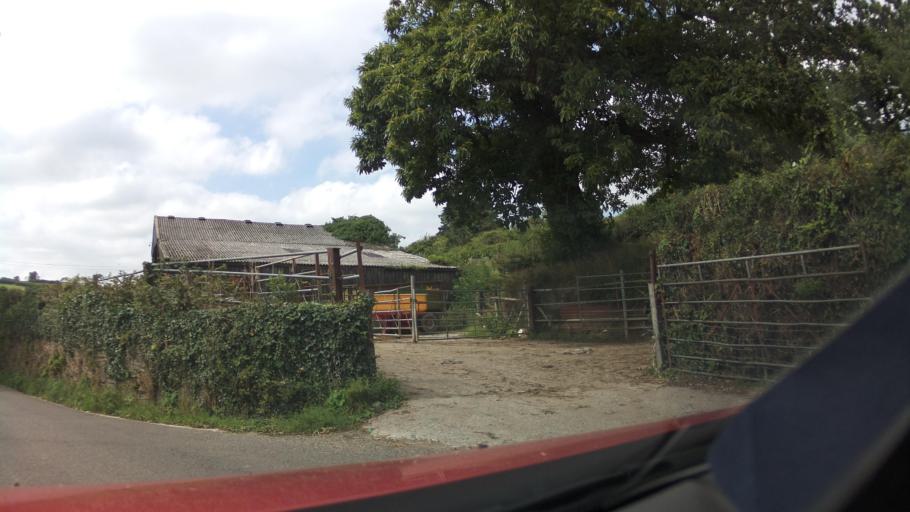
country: GB
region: England
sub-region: Devon
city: South Brent
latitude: 50.4069
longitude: -3.8202
